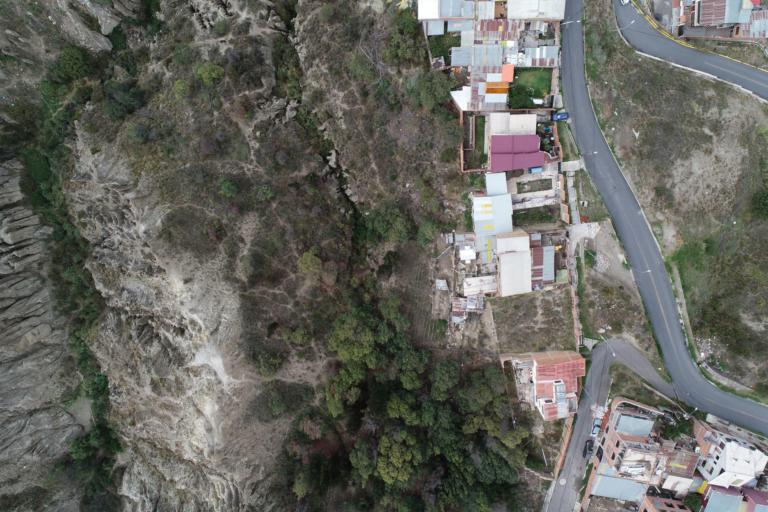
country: BO
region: La Paz
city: La Paz
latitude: -16.5161
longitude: -68.1086
